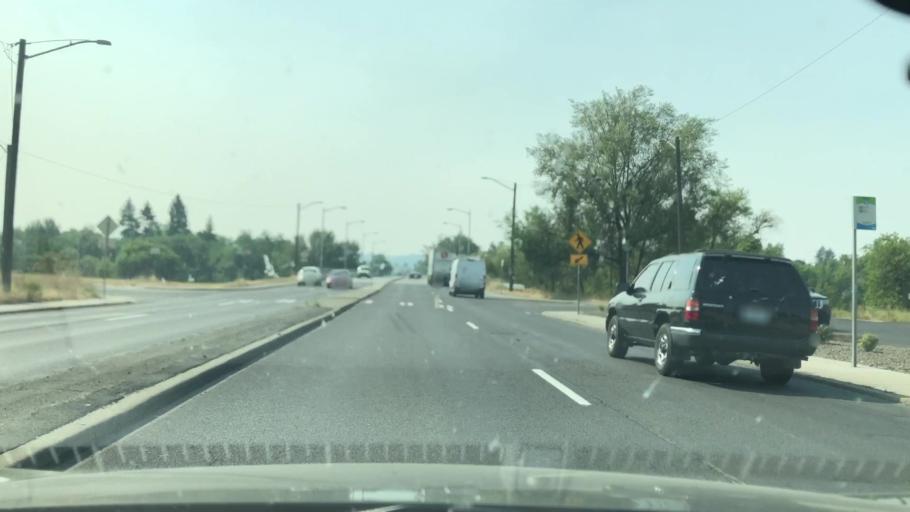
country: US
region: Washington
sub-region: Spokane County
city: Spokane
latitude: 47.6799
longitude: -117.3637
